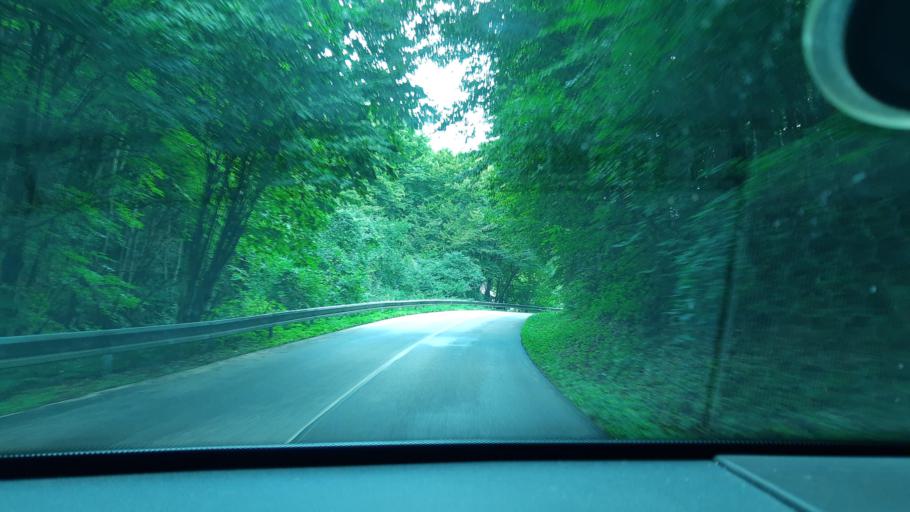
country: SK
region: Trnavsky
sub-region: Okres Trnava
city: Piestany
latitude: 48.6458
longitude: 17.9382
